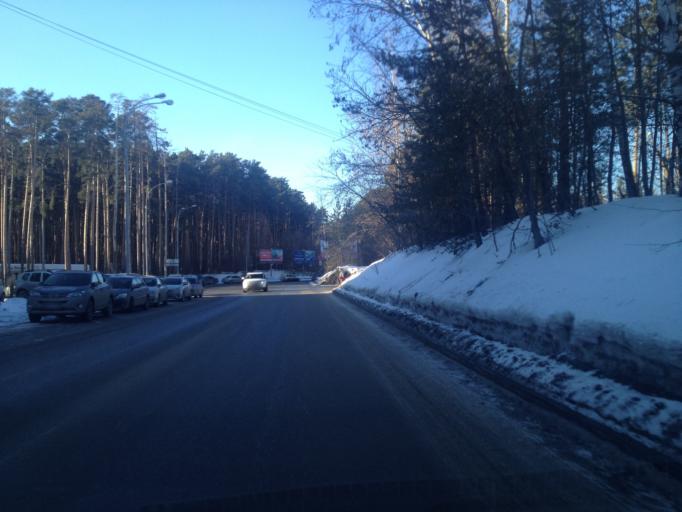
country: RU
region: Sverdlovsk
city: Sovkhoznyy
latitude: 56.8138
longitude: 60.5366
